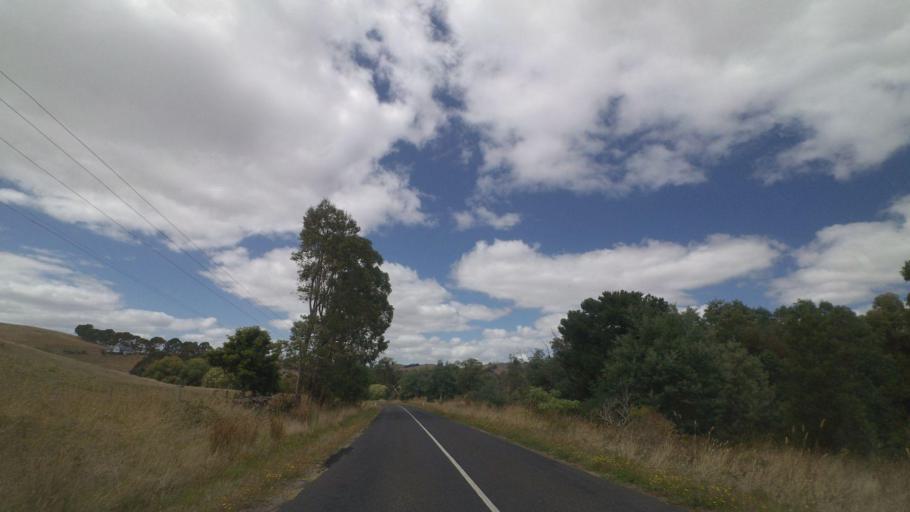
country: AU
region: Victoria
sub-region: Cardinia
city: Bunyip
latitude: -38.3543
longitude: 145.7021
